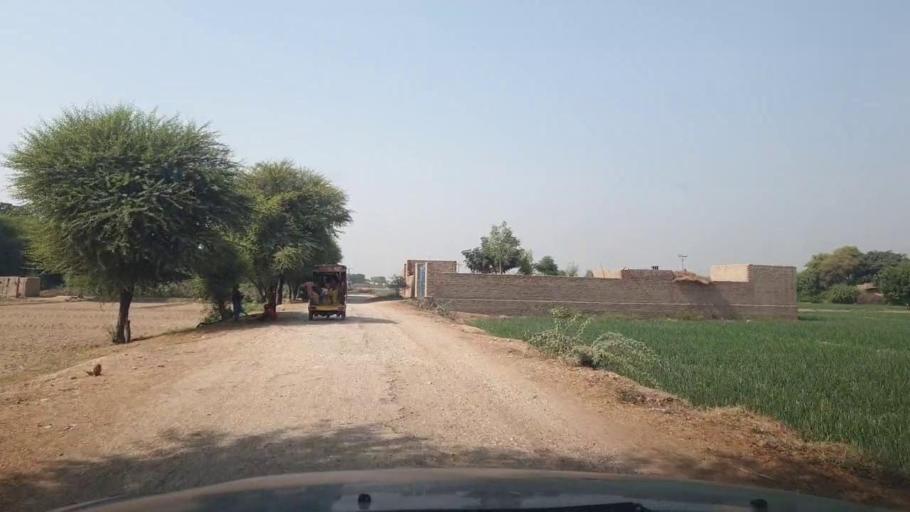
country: PK
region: Sindh
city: Bhit Shah
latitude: 25.7368
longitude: 68.5049
